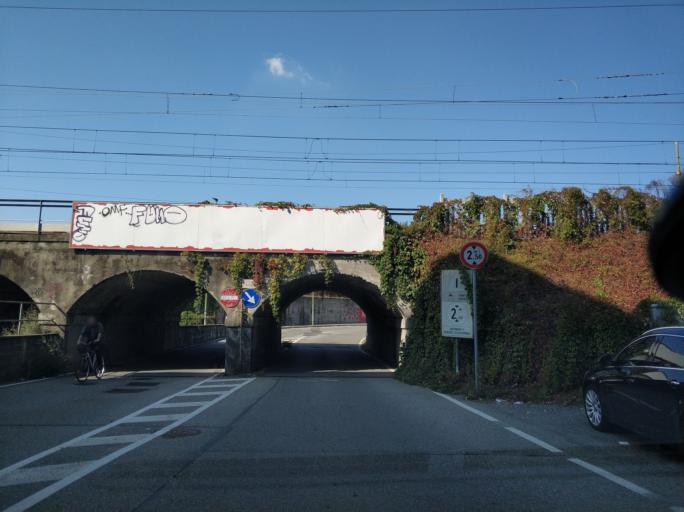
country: IT
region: Piedmont
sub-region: Provincia di Torino
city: Settimo Torinese
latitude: 45.1435
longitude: 7.7761
